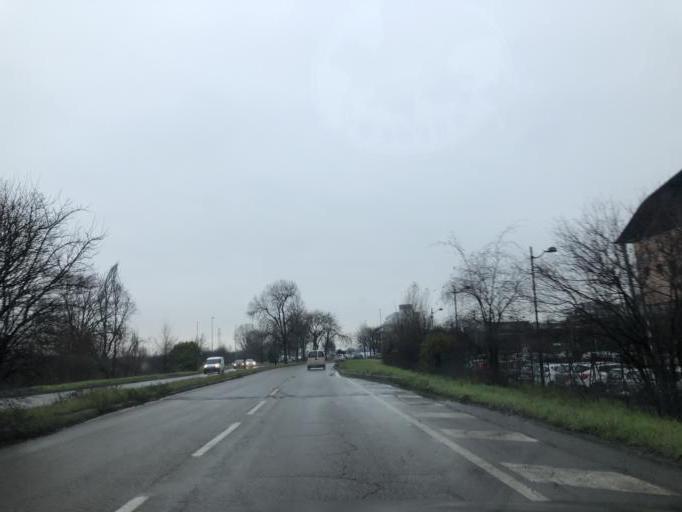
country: IT
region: Emilia-Romagna
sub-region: Provincia di Modena
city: Modena
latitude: 44.6375
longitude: 10.8896
